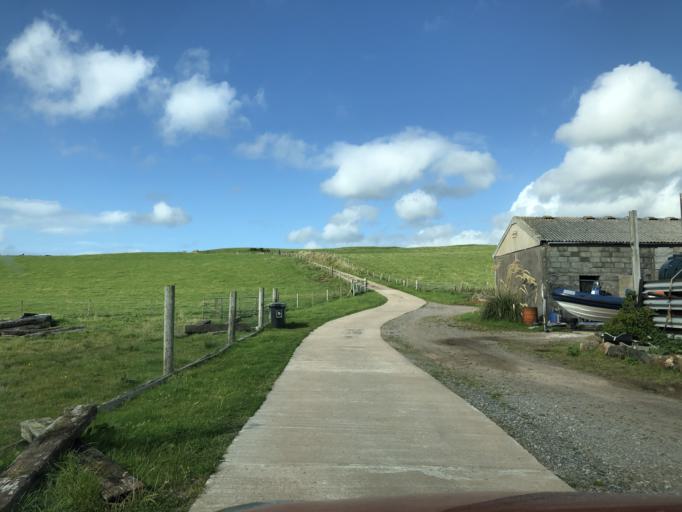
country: GB
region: Scotland
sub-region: Argyll and Bute
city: Campbeltown
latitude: 55.3105
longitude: -5.6063
